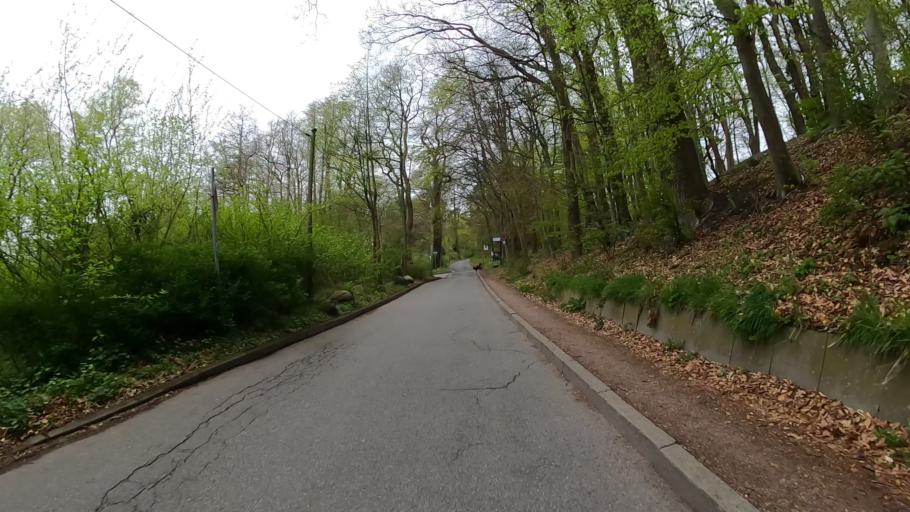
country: DE
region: Schleswig-Holstein
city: Wedel
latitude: 53.5653
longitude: 9.7624
